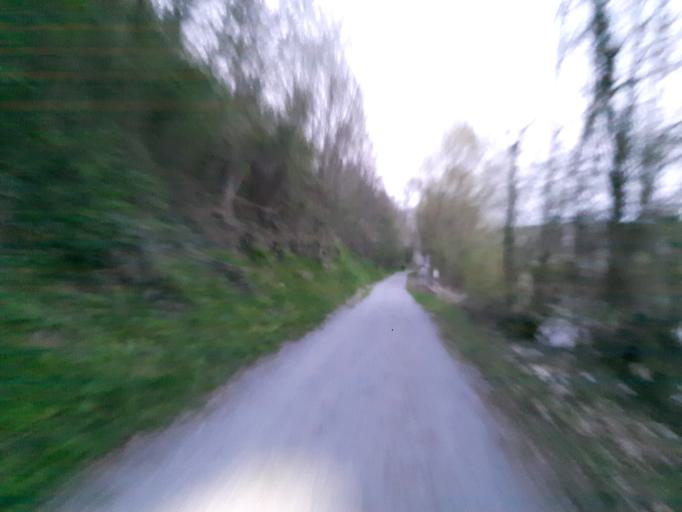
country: DE
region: Baden-Wuerttemberg
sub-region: Regierungsbezirk Stuttgart
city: Neckarwestheim
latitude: 49.0546
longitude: 9.1748
